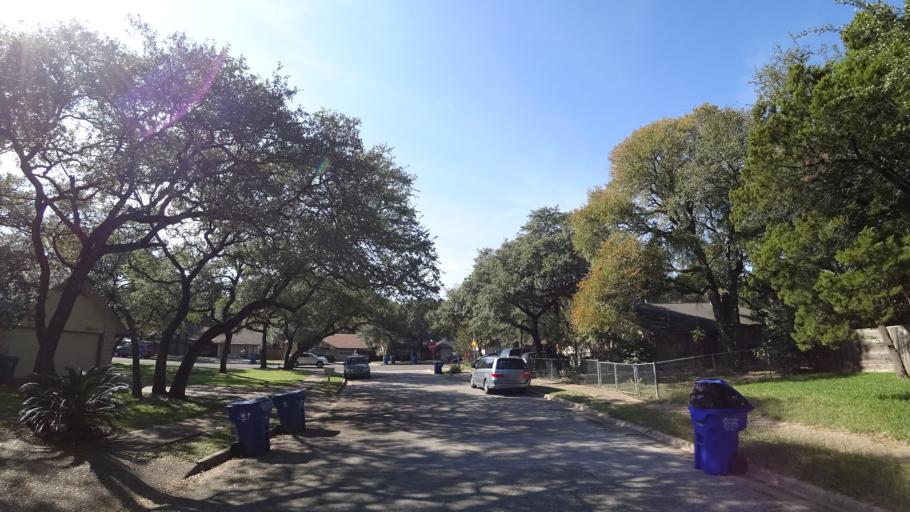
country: US
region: Texas
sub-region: Williamson County
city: Anderson Mill
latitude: 30.4519
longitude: -97.7958
